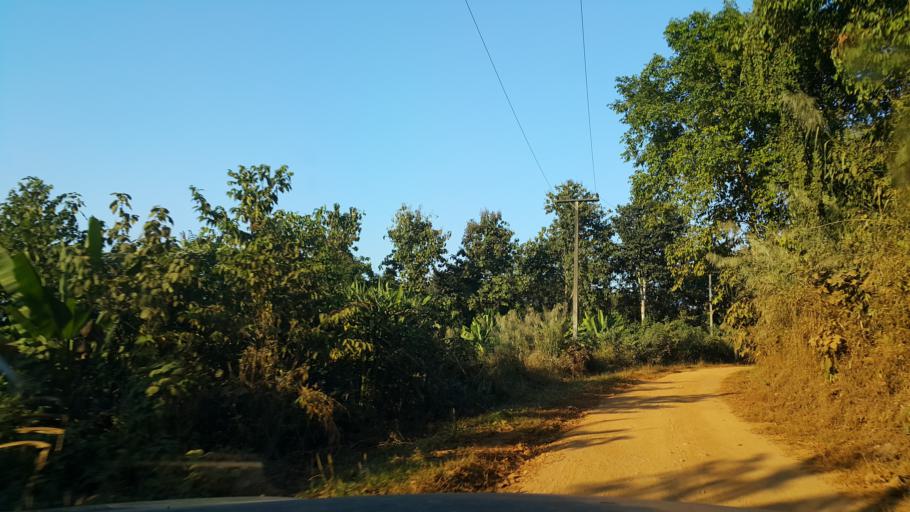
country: TH
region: Sukhothai
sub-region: Amphoe Si Satchanalai
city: Si Satchanalai
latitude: 17.6106
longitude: 99.6197
